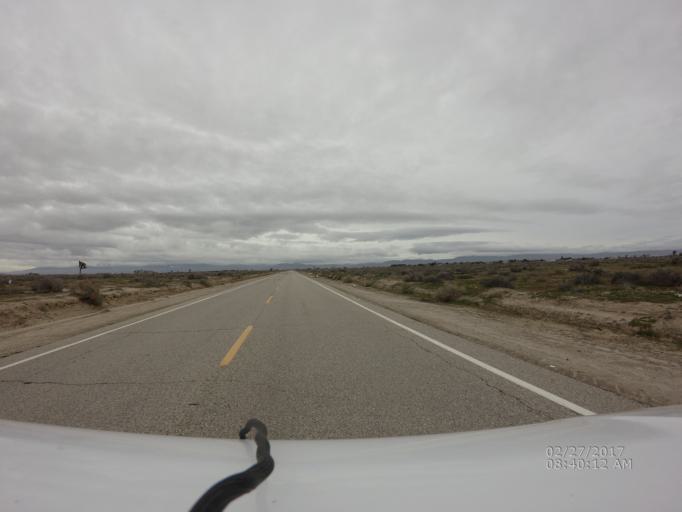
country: US
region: California
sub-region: Los Angeles County
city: Lancaster
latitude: 34.7264
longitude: -118.0591
